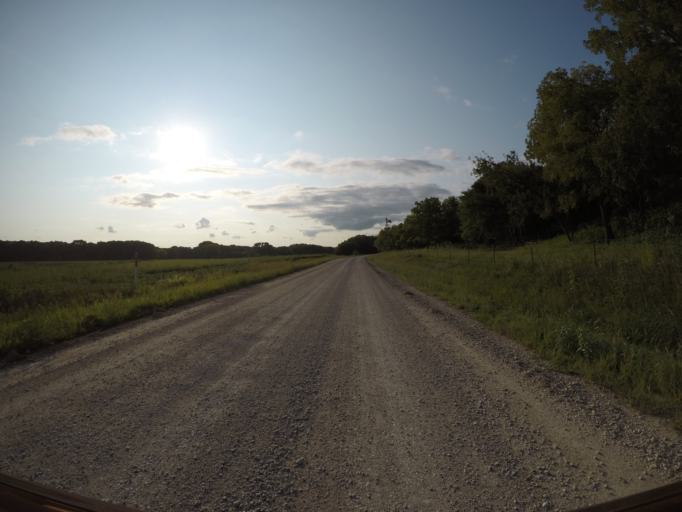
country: US
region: Kansas
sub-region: Wabaunsee County
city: Alma
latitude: 38.9677
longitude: -96.2602
